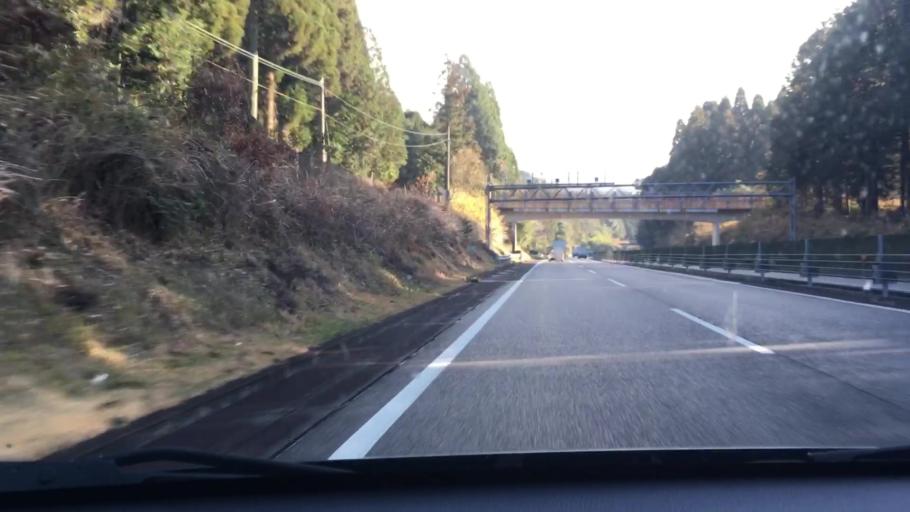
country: JP
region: Kagoshima
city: Okuchi-shinohara
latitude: 32.0022
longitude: 130.7570
